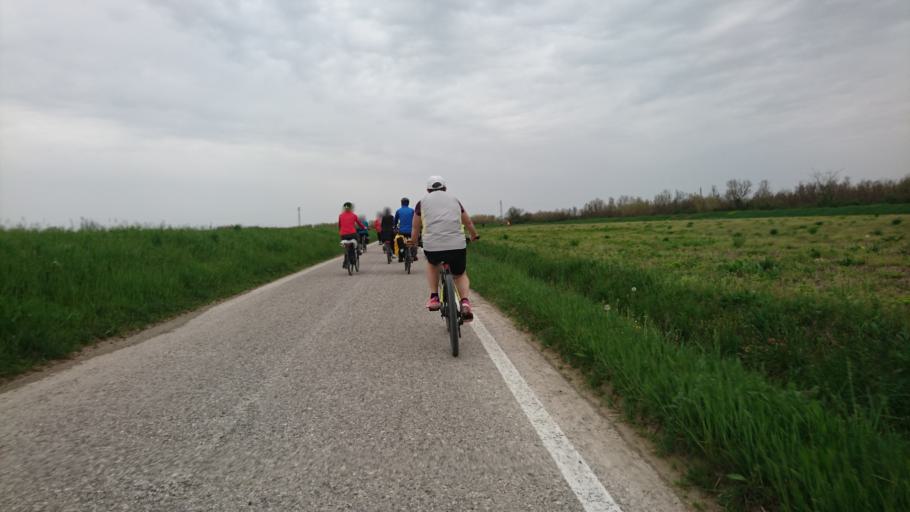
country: IT
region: Veneto
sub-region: Provincia di Venezia
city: Cesarolo
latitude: 45.6906
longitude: 12.9860
